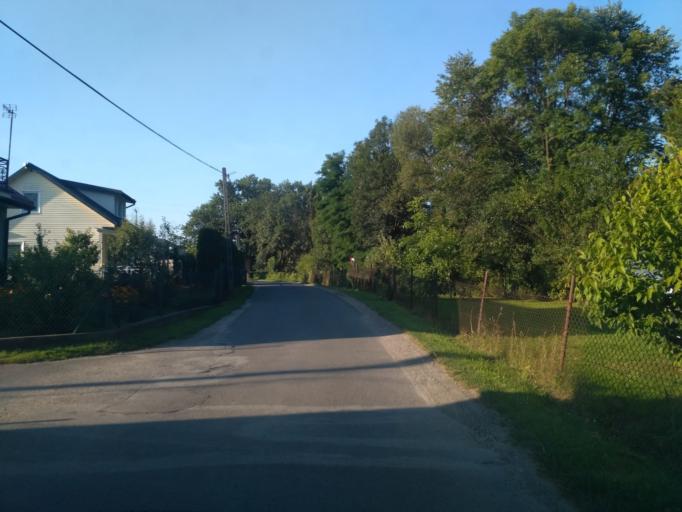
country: PL
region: Subcarpathian Voivodeship
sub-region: Powiat krosnienski
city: Dukla
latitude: 49.5572
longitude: 21.6888
